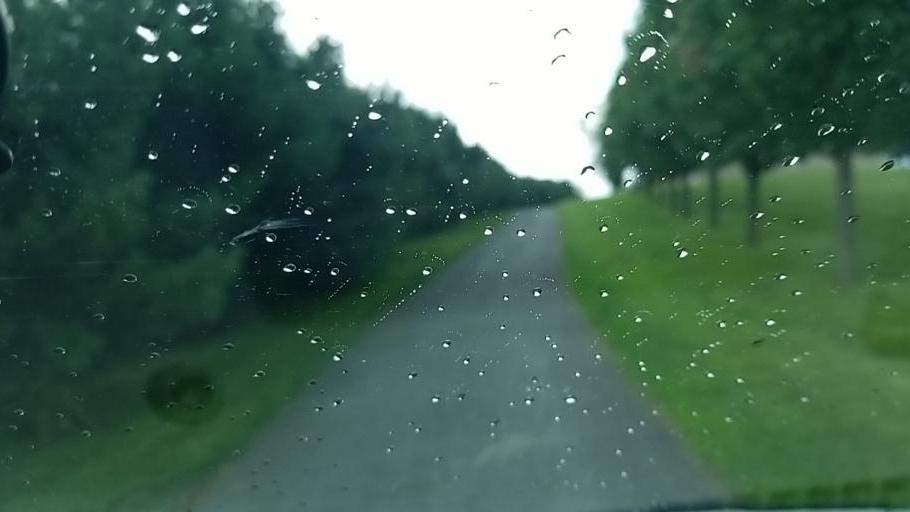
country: US
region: Pennsylvania
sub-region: Dauphin County
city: Elizabethville
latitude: 40.5821
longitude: -76.8764
